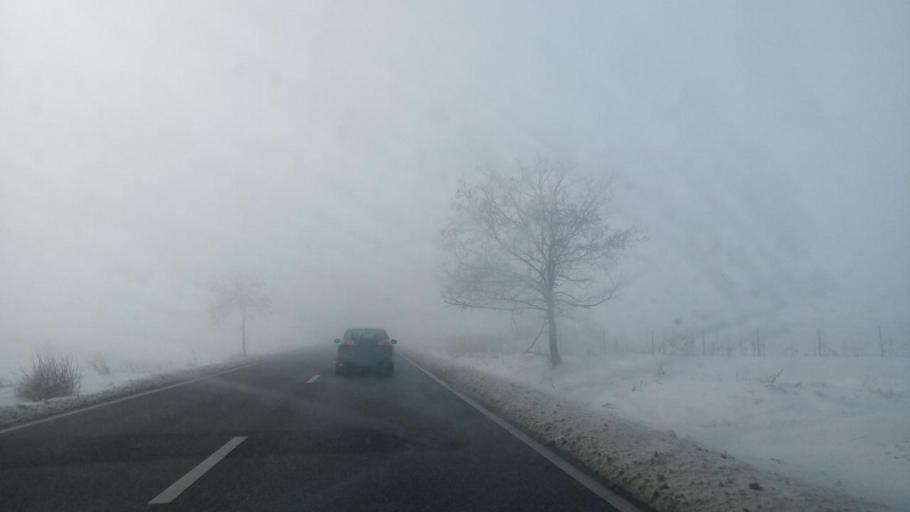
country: RO
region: Suceava
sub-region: Comuna Radaseni
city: Radaseni
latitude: 47.4518
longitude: 26.2460
